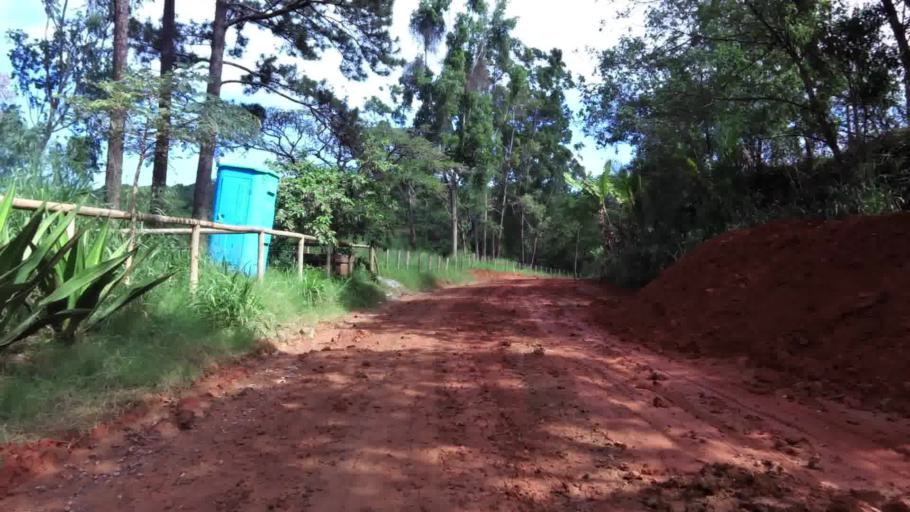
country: BR
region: Espirito Santo
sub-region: Piuma
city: Piuma
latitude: -20.8126
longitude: -40.6712
